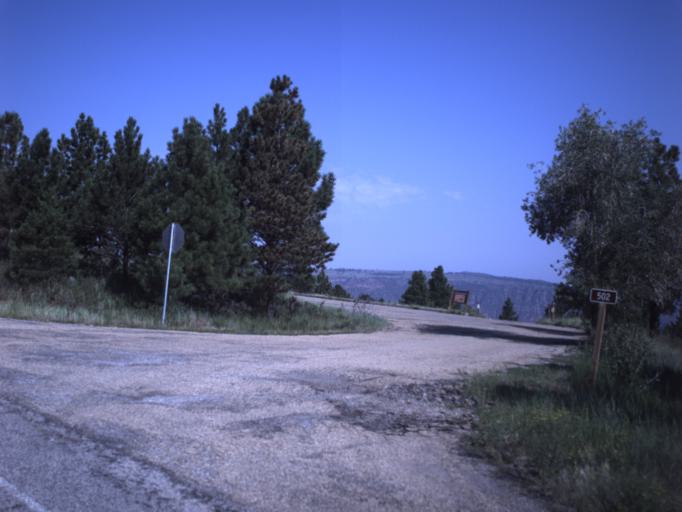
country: US
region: Utah
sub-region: Daggett County
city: Manila
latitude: 40.8720
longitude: -109.4953
